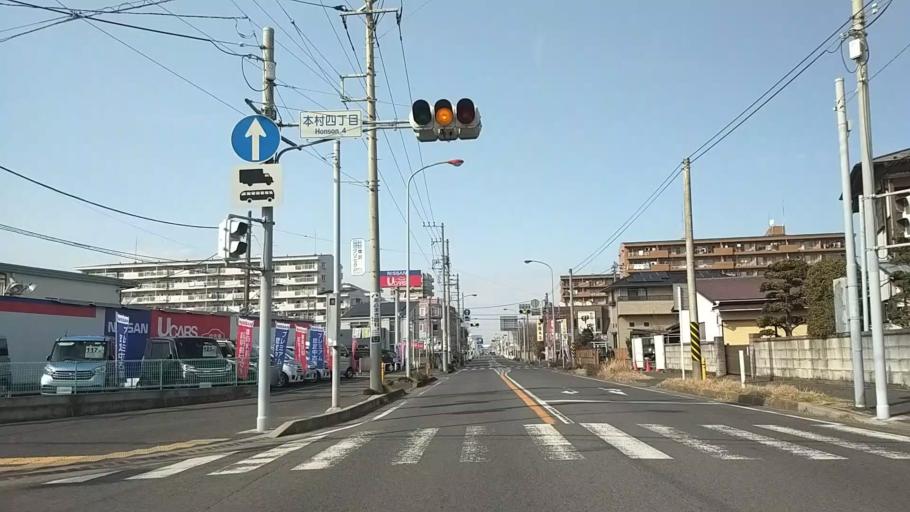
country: JP
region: Kanagawa
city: Chigasaki
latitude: 35.3381
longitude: 139.4138
